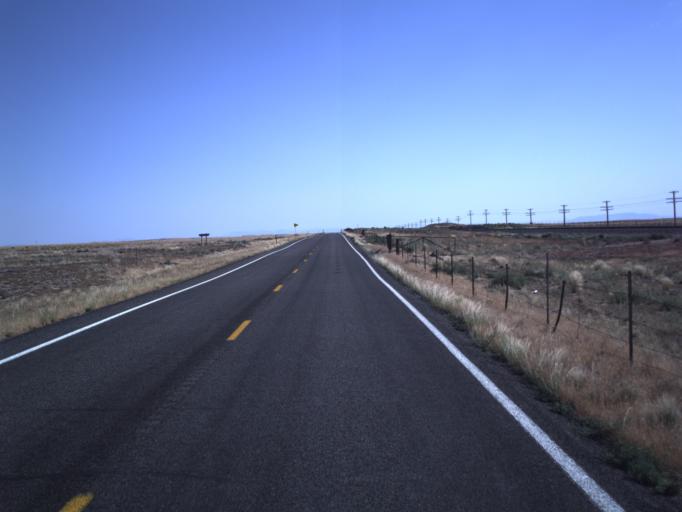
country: US
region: Utah
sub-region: Millard County
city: Delta
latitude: 38.9808
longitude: -112.7952
